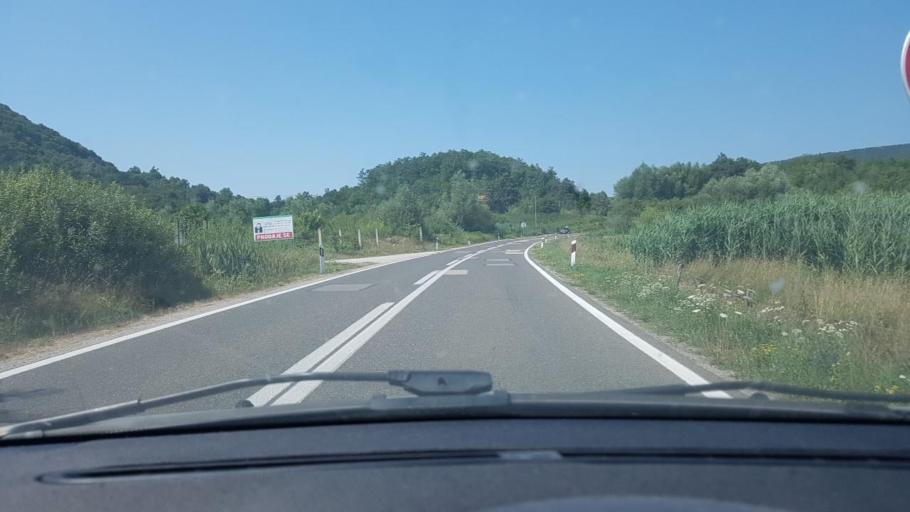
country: BA
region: Federation of Bosnia and Herzegovina
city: Bihac
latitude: 44.7601
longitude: 15.9443
